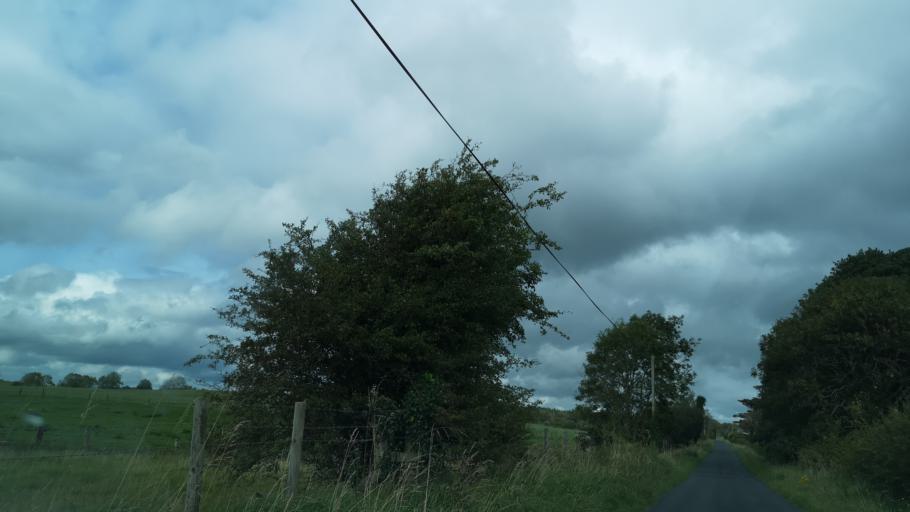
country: IE
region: Connaught
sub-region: County Galway
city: Athenry
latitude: 53.2850
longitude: -8.6667
